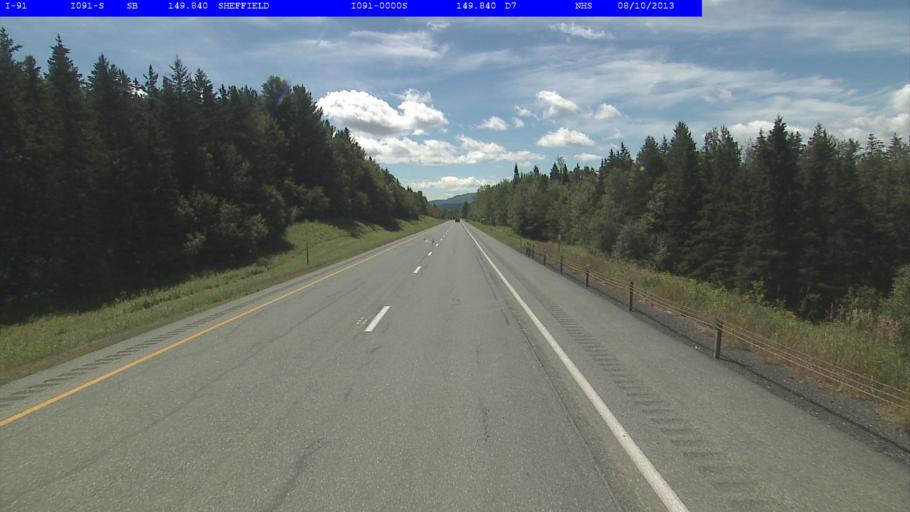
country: US
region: Vermont
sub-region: Caledonia County
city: Lyndonville
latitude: 44.6623
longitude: -72.1343
